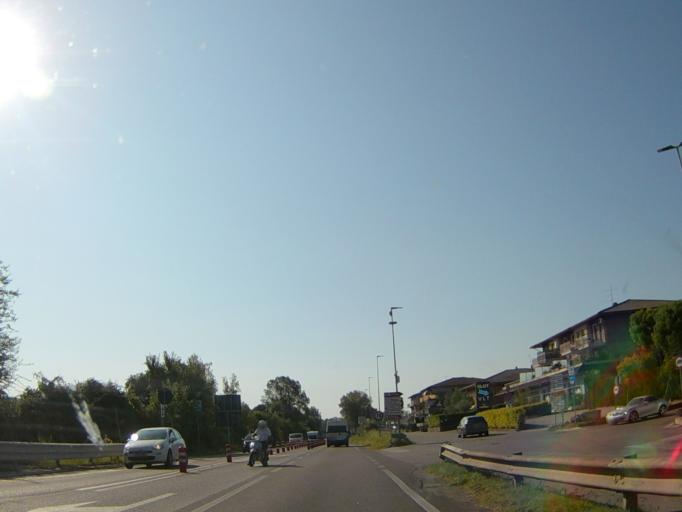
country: IT
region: Veneto
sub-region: Provincia di Verona
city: Peschiera del Garda
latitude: 45.4382
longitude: 10.6789
